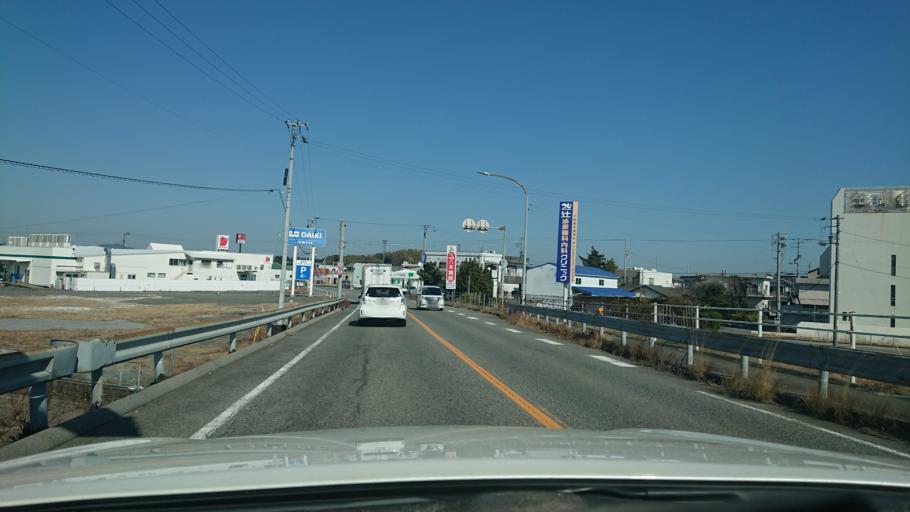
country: JP
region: Tokushima
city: Anan
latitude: 33.9601
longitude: 134.6235
